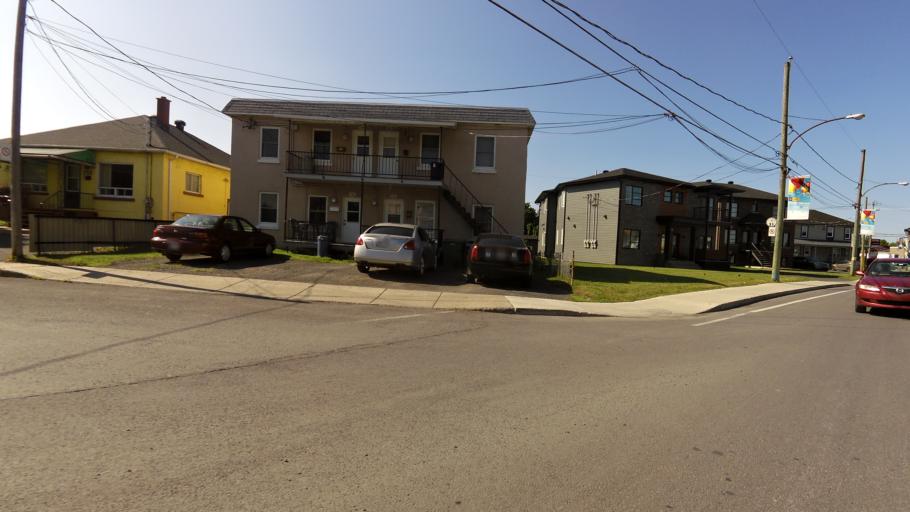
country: CA
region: Quebec
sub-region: Monteregie
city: Saint-Jean-sur-Richelieu
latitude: 45.3043
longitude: -73.2906
